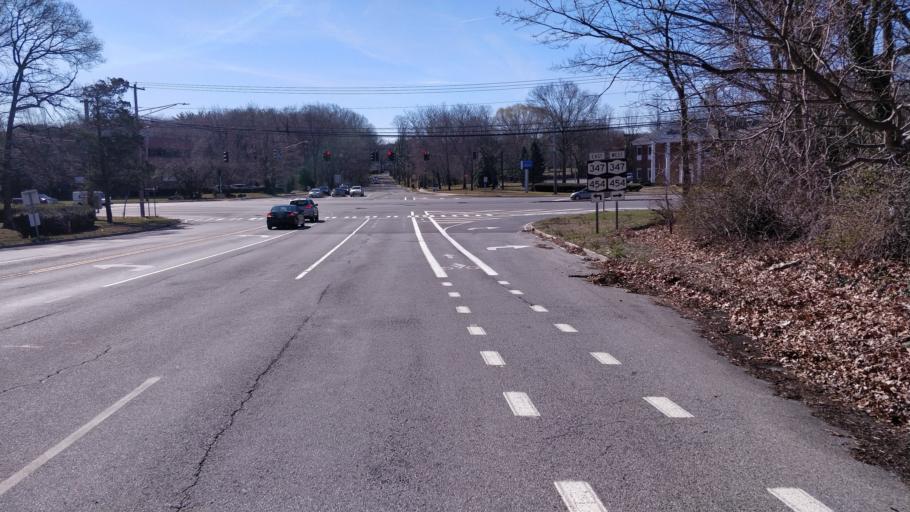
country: US
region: New York
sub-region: Suffolk County
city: Hauppauge
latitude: 40.8260
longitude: -73.2350
